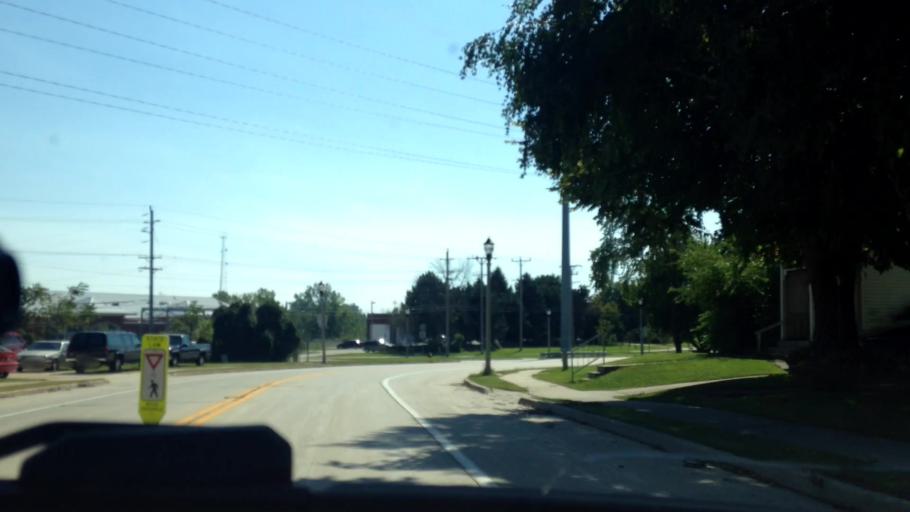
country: US
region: Wisconsin
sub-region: Ozaukee County
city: Port Washington
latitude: 43.3847
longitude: -87.8858
